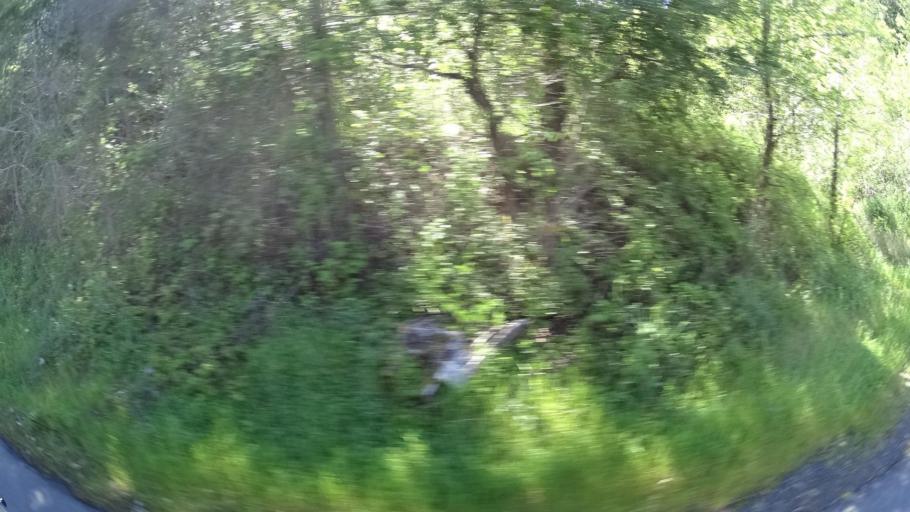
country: US
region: California
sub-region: Humboldt County
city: Rio Dell
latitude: 40.2300
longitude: -124.1424
